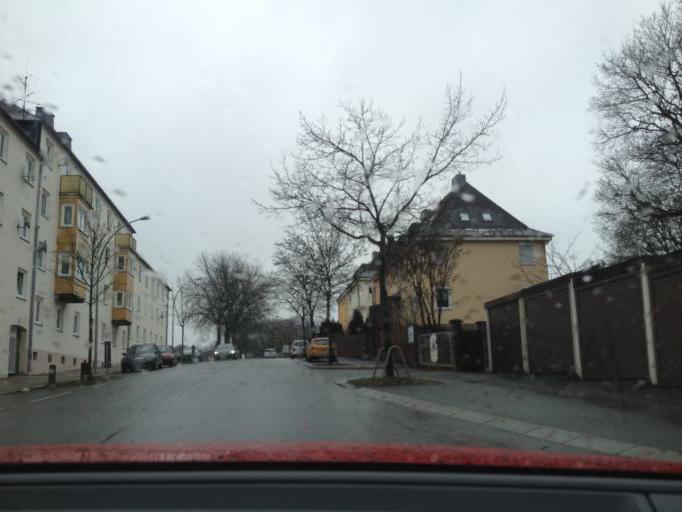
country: DE
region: Bavaria
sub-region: Upper Franconia
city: Hof
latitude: 50.3135
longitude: 11.9317
